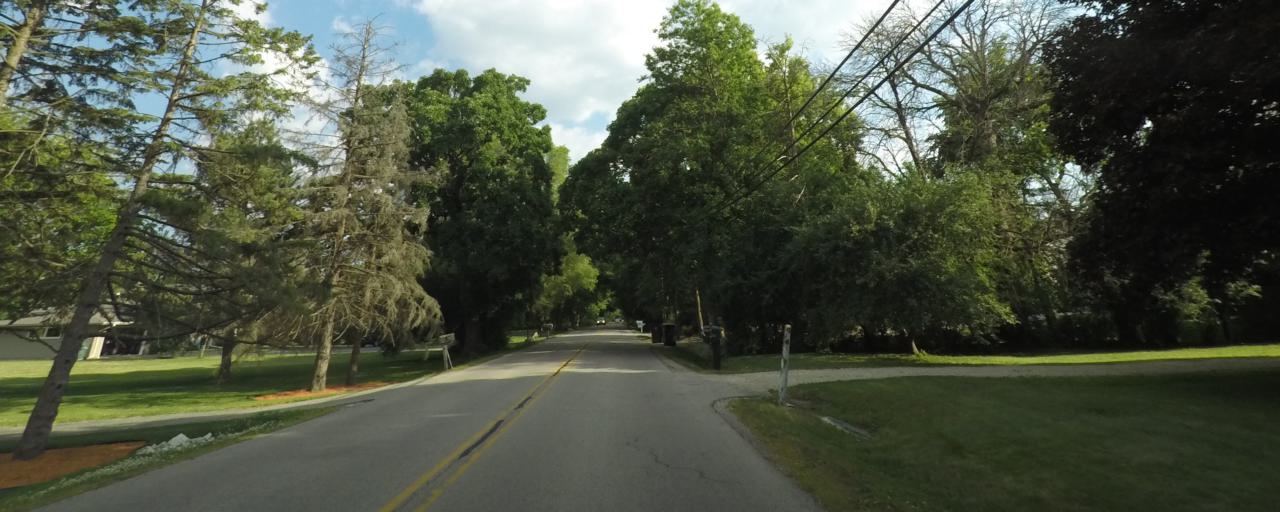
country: US
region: Wisconsin
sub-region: Milwaukee County
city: Hales Corners
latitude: 42.9414
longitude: -88.0284
